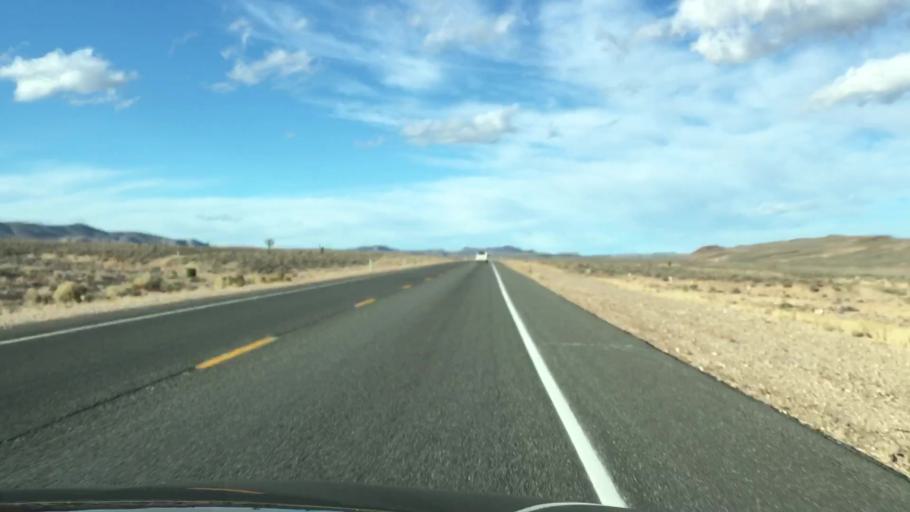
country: US
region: Nevada
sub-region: Esmeralda County
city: Goldfield
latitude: 37.5426
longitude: -117.1955
